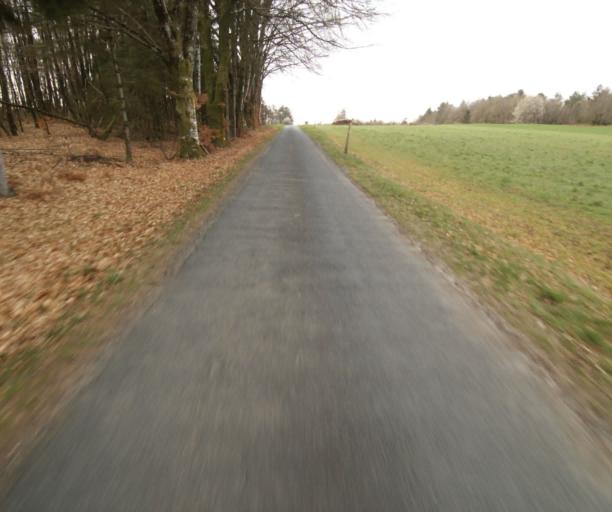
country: FR
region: Limousin
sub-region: Departement de la Correze
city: Correze
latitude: 45.4460
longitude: 1.8205
